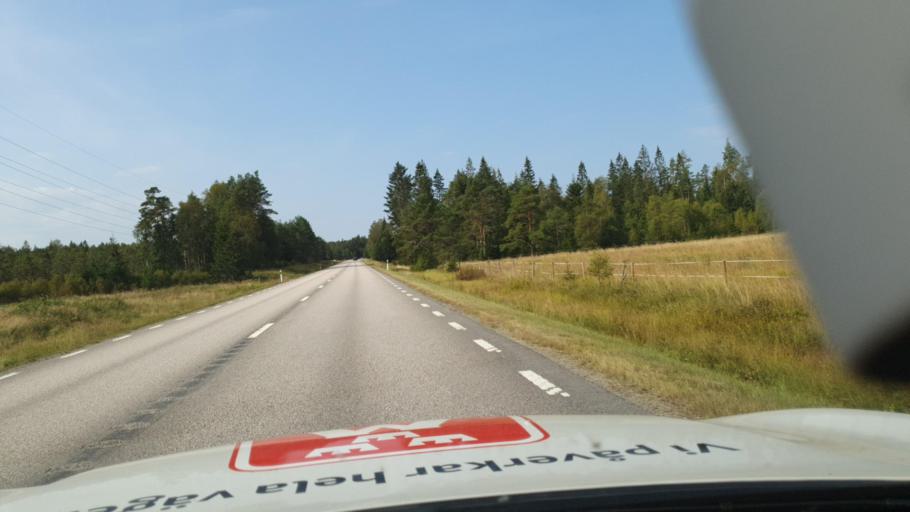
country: SE
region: Vaestra Goetaland
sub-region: Dals-Ed Kommun
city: Ed
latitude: 58.8455
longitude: 11.7575
